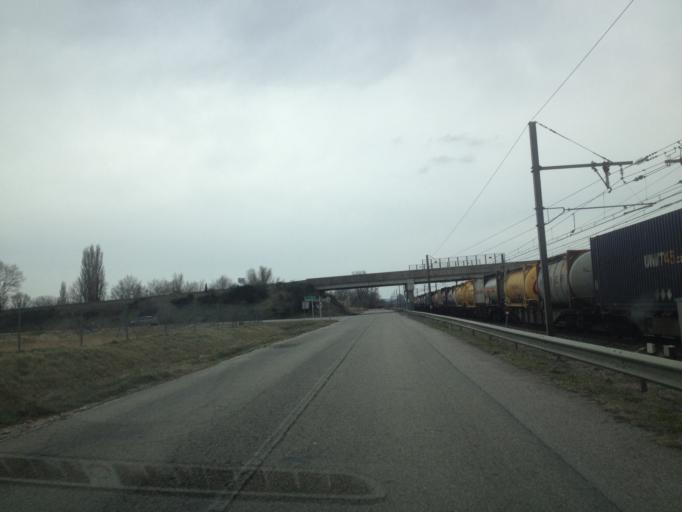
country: FR
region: Provence-Alpes-Cote d'Azur
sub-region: Departement du Vaucluse
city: Courthezon
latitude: 44.1019
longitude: 4.8867
